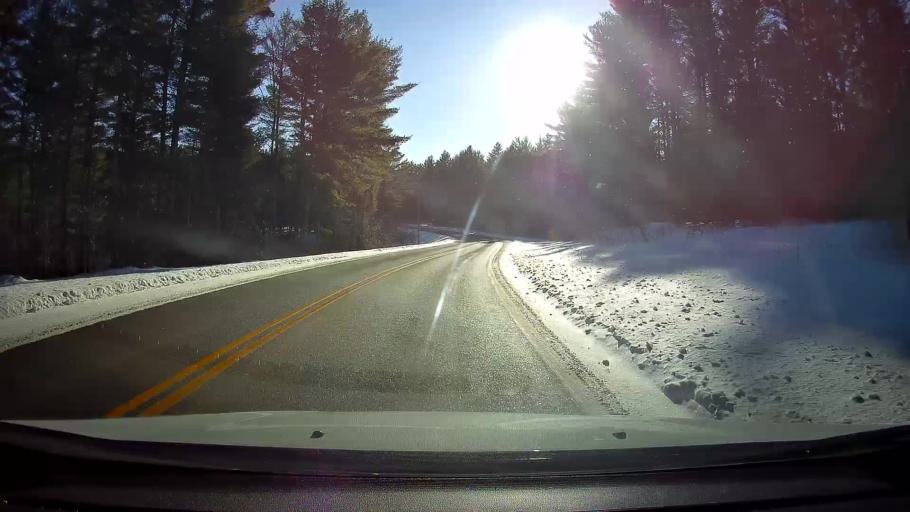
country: US
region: Wisconsin
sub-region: Sawyer County
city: Little Round Lake
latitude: 46.1131
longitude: -91.3164
